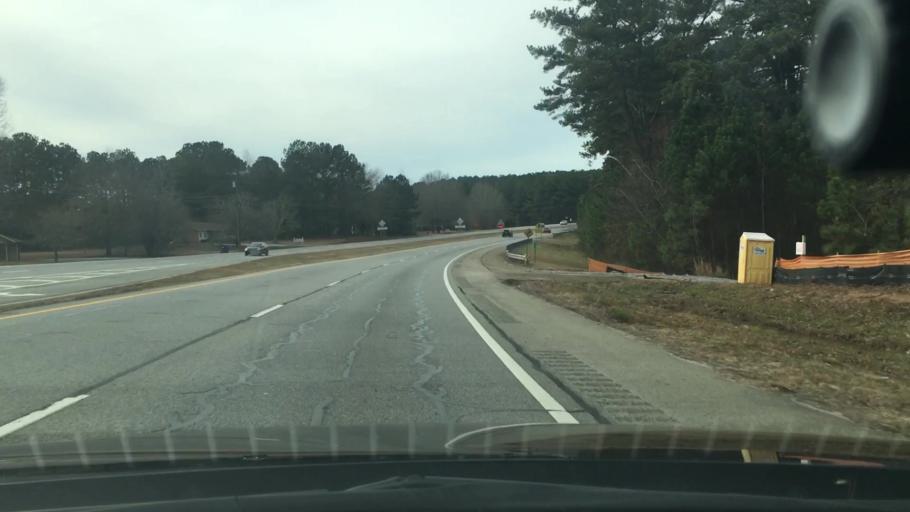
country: US
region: Georgia
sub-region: Fayette County
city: Peachtree City
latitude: 33.3992
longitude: -84.6562
